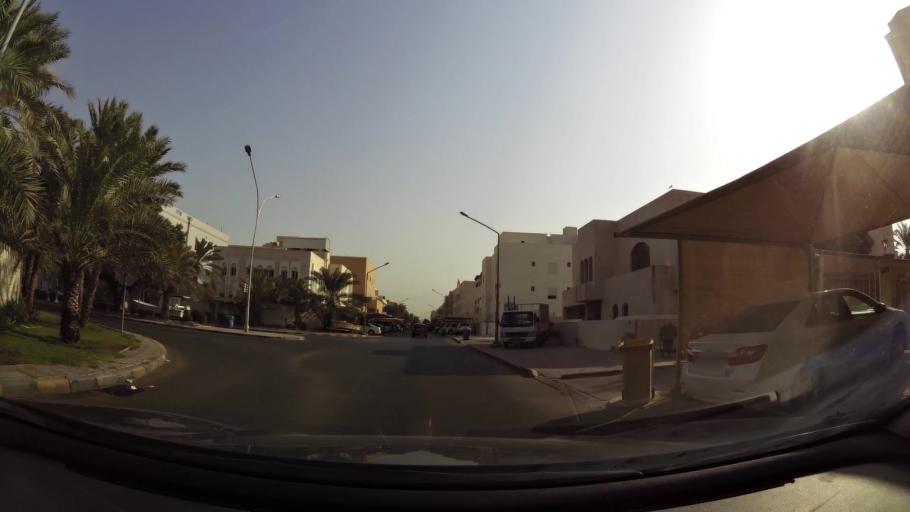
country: KW
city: Bayan
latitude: 29.3135
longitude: 48.0456
